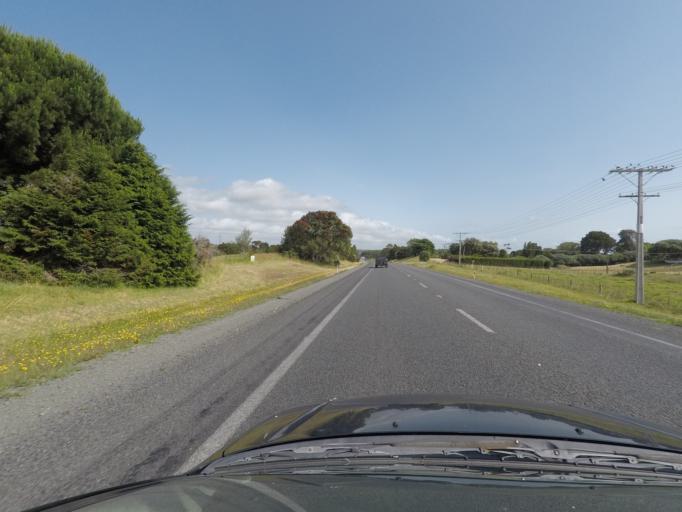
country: NZ
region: Northland
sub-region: Whangarei
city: Ruakaka
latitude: -35.9129
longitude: 174.4508
